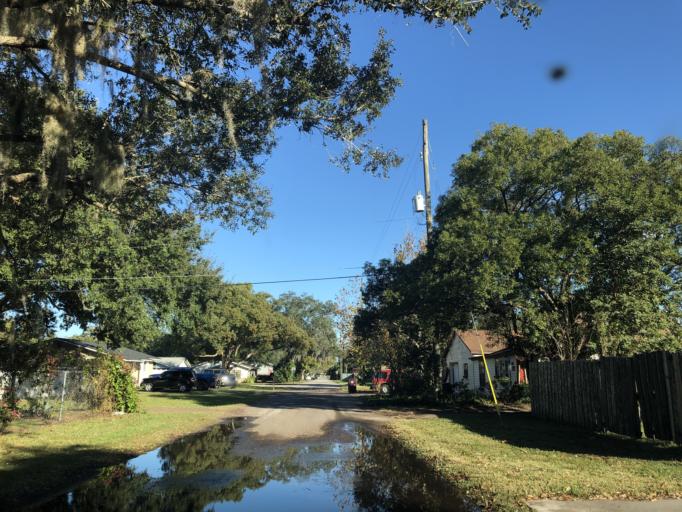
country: US
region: Florida
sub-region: Osceola County
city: Saint Cloud
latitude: 28.2507
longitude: -81.2734
